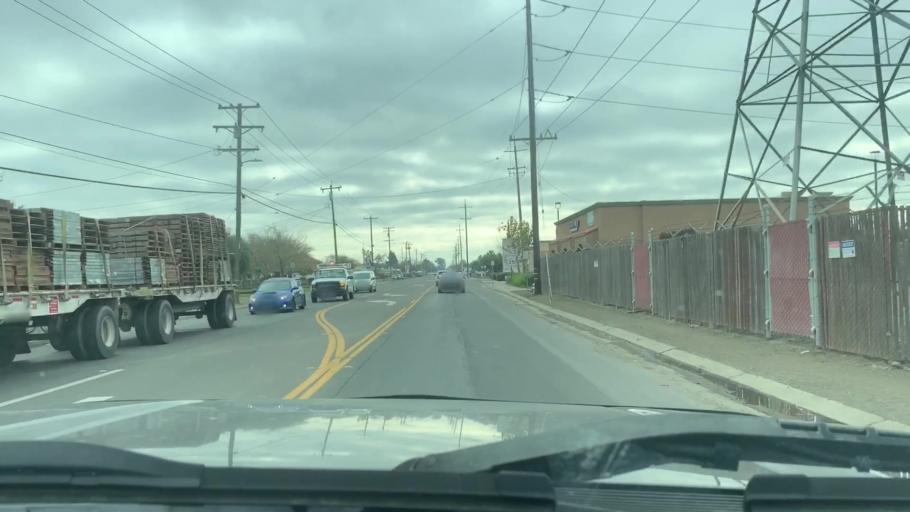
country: US
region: California
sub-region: Merced County
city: Los Banos
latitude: 37.0664
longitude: -120.8353
